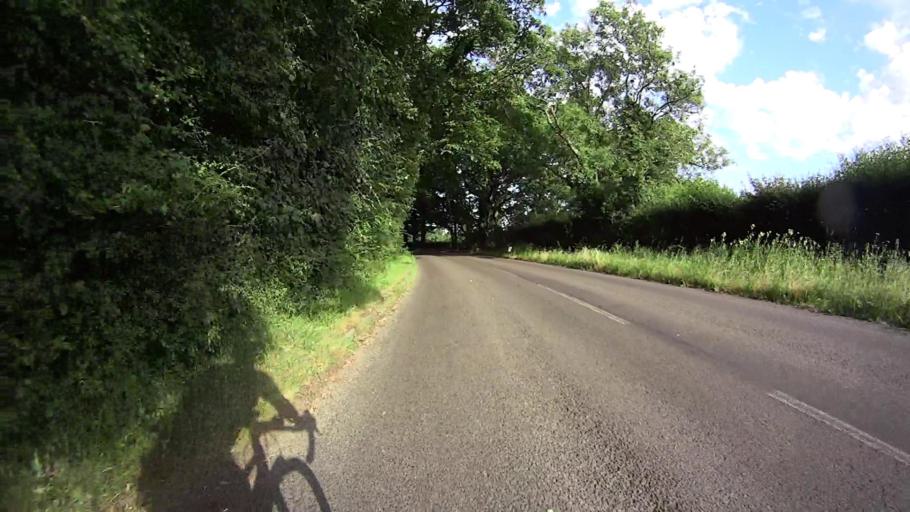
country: GB
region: England
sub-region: West Sussex
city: Bewbush
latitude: 51.1208
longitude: -0.2411
